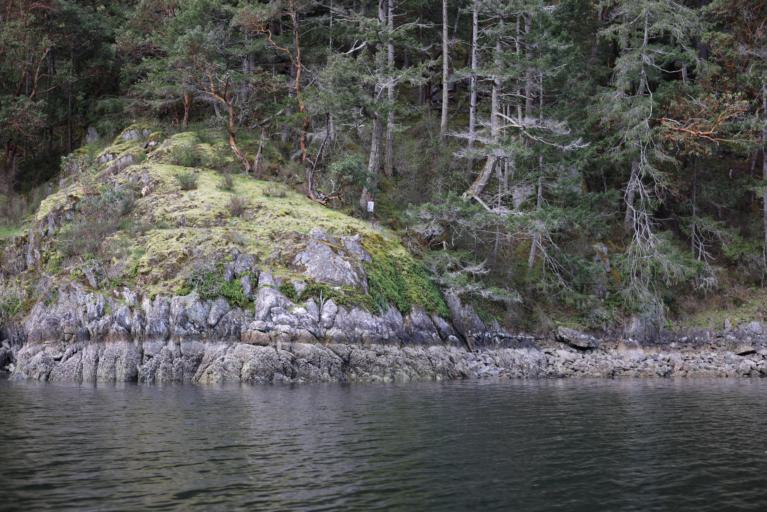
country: CA
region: British Columbia
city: Langford
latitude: 48.5035
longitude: -123.5517
